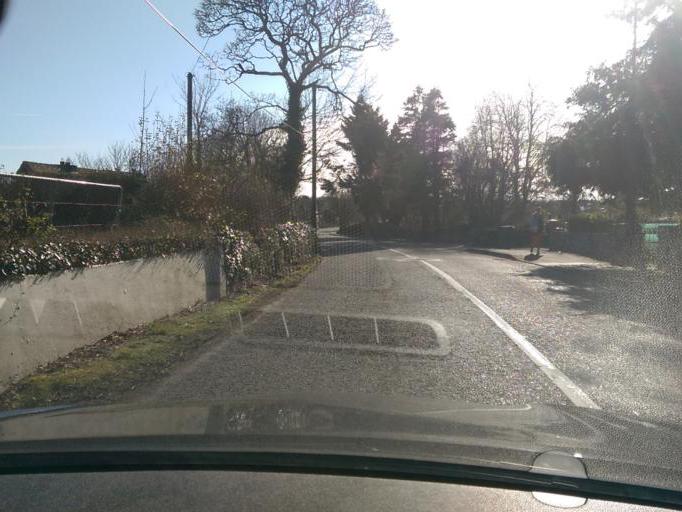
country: IE
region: Connaught
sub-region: County Galway
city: Oranmore
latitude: 53.2573
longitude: -8.9348
